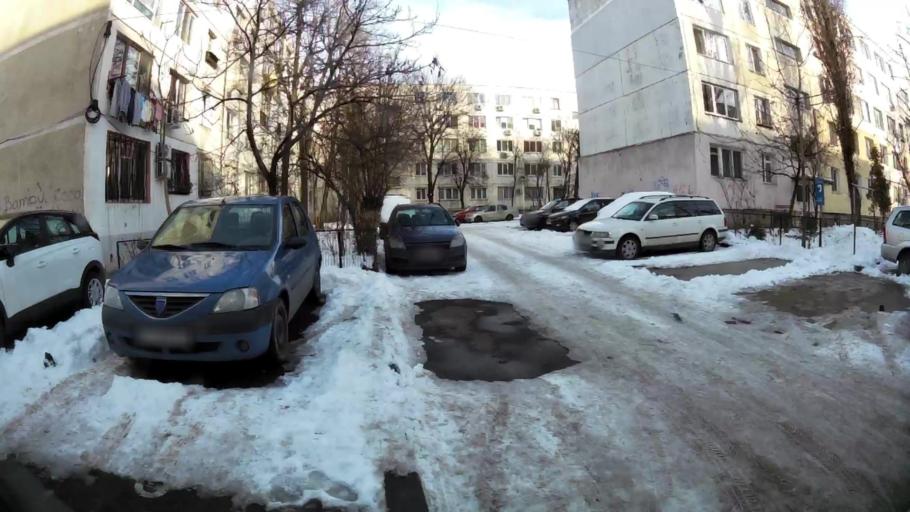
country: RO
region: Bucuresti
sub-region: Municipiul Bucuresti
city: Bucuresti
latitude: 44.3867
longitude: 26.0961
